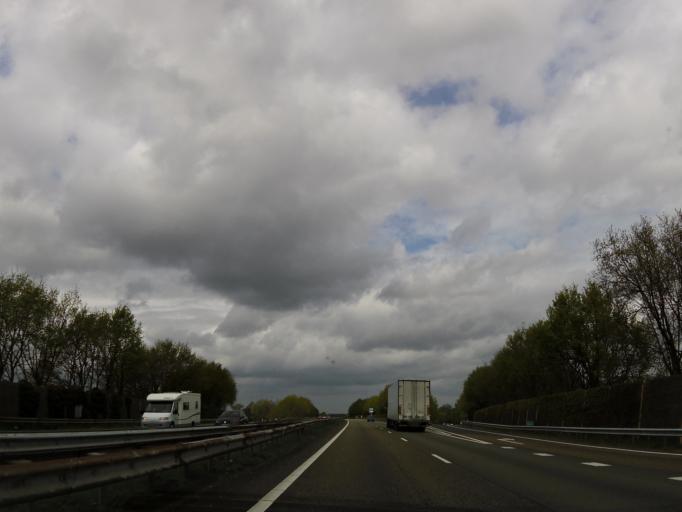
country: NL
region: North Brabant
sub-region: Gemeente Cranendonck
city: Cranendonck
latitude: 51.3096
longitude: 5.6090
